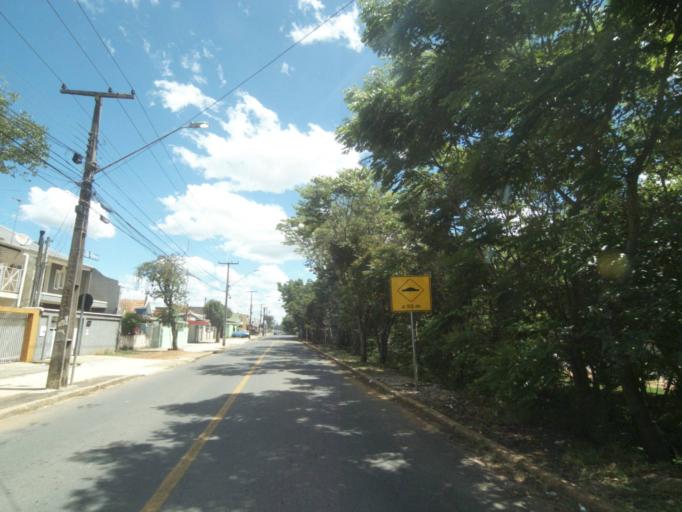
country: BR
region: Parana
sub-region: Curitiba
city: Curitiba
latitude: -25.5013
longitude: -49.3252
